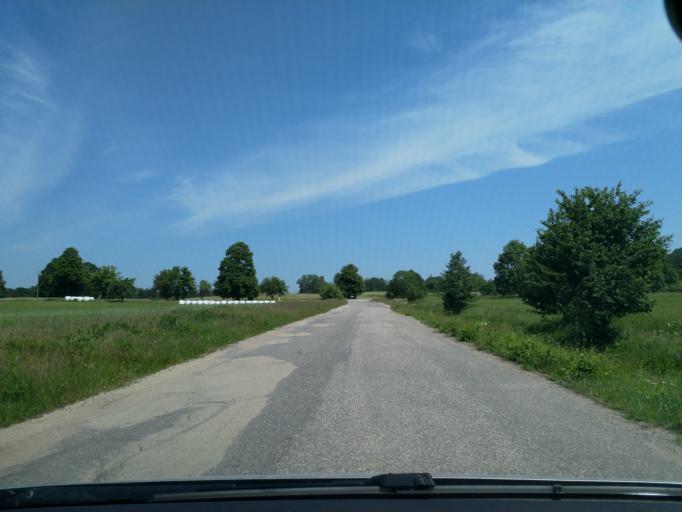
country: LV
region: Kuldigas Rajons
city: Kuldiga
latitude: 56.9542
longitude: 22.0132
